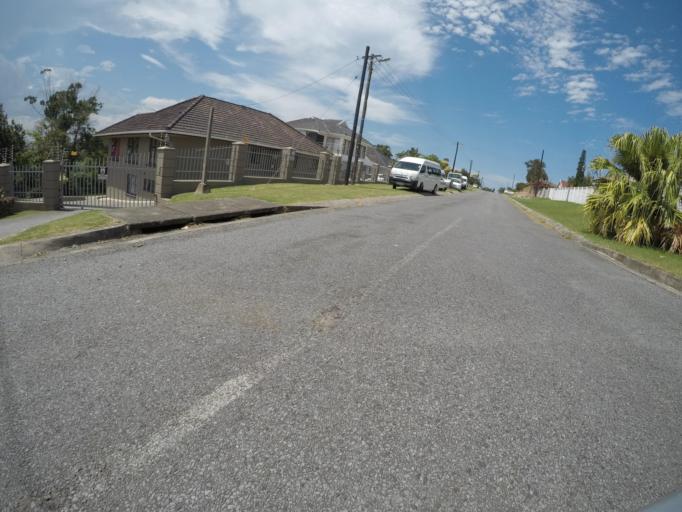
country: ZA
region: Eastern Cape
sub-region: Buffalo City Metropolitan Municipality
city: East London
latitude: -33.0314
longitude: 27.8633
